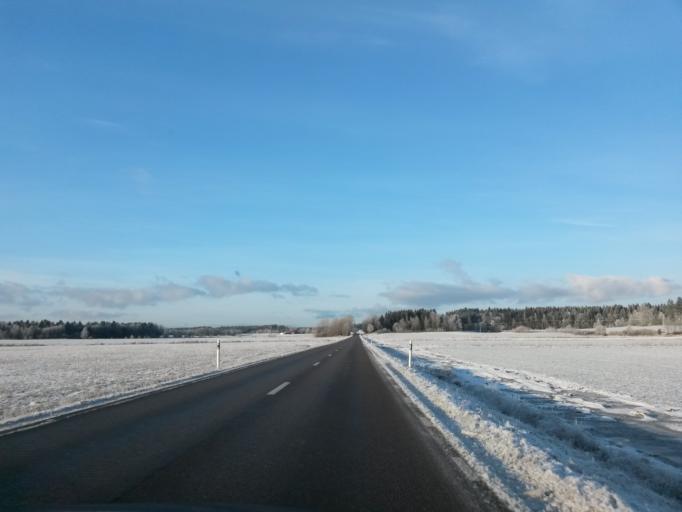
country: SE
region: Vaestra Goetaland
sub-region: Vargarda Kommun
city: Vargarda
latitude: 58.0477
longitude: 12.7836
